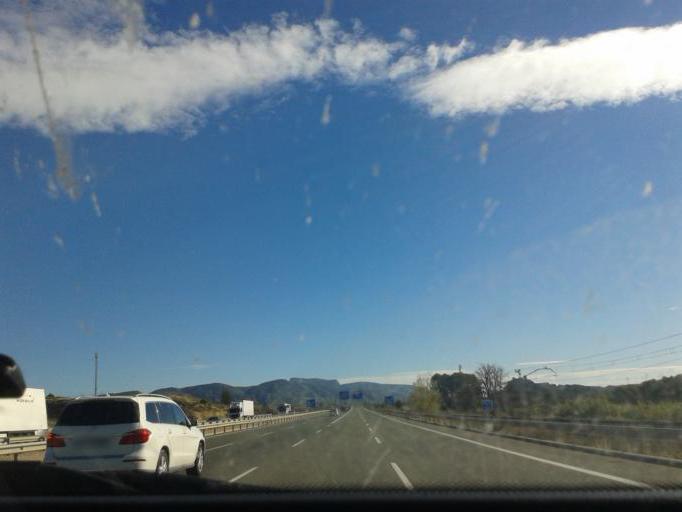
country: ES
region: Valencia
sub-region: Provincia de Alicante
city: Sax
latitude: 38.5595
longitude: -0.8289
